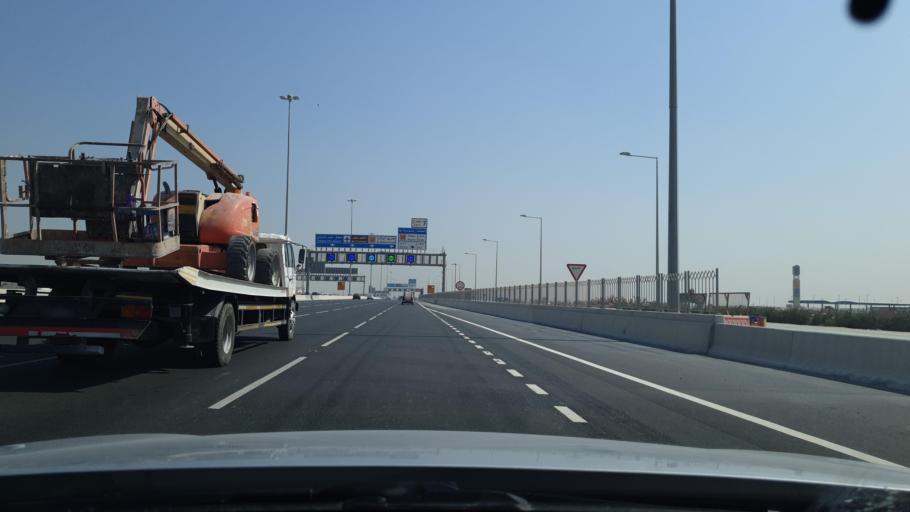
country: QA
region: Baladiyat ad Dawhah
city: Doha
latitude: 25.2237
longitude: 51.5482
